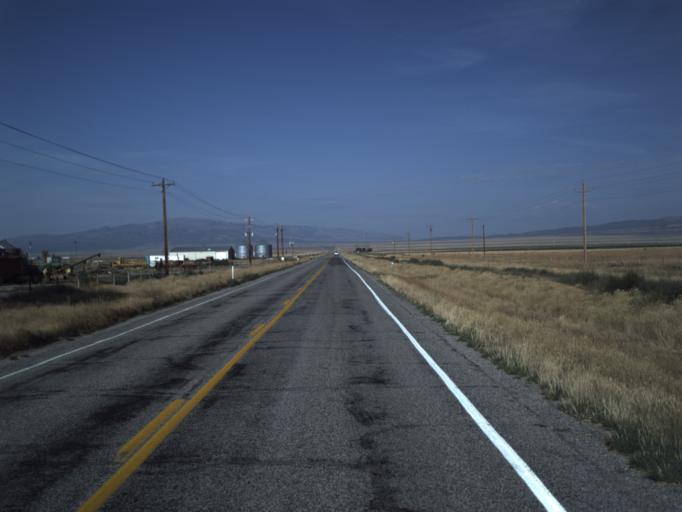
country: US
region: Idaho
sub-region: Oneida County
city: Malad City
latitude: 41.9667
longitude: -112.8988
